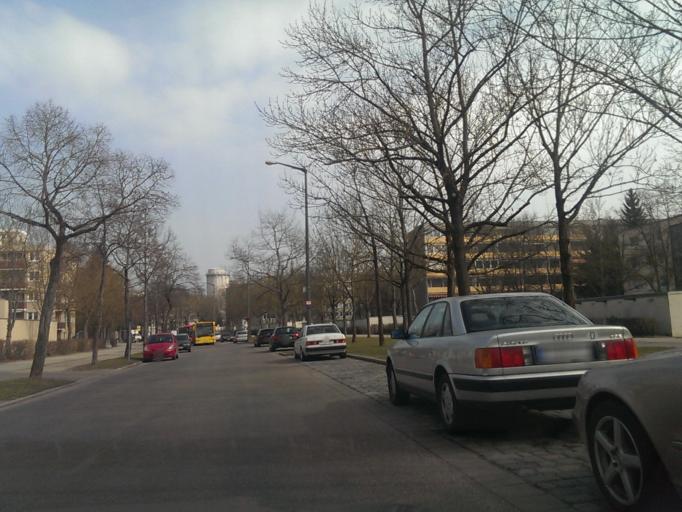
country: DE
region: Bavaria
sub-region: Upper Palatinate
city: Regensburg
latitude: 49.0337
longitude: 12.1260
